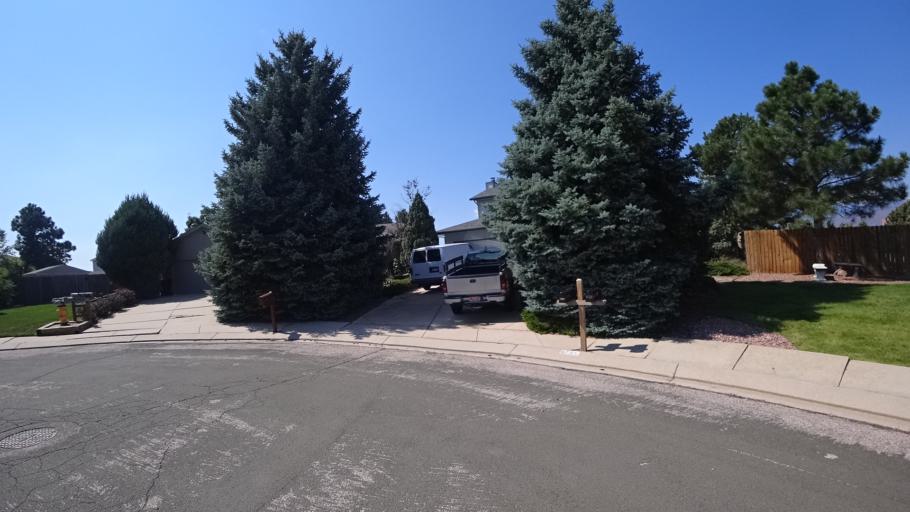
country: US
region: Colorado
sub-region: El Paso County
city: Black Forest
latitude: 38.9573
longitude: -104.7740
